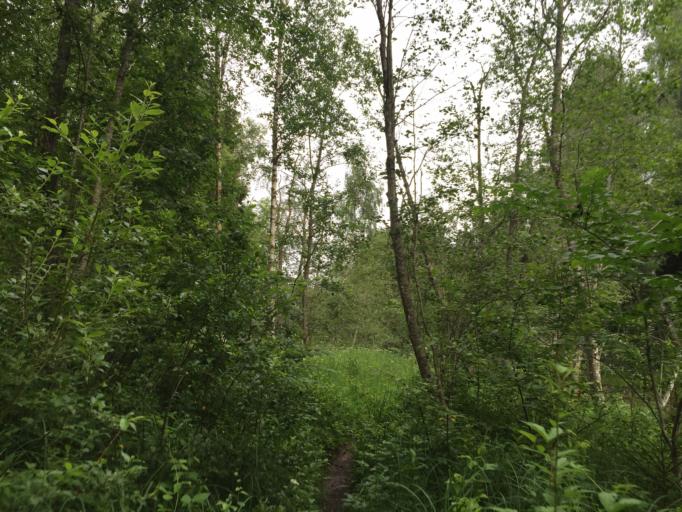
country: LV
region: Ligatne
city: Ligatne
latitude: 57.2379
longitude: 25.1530
